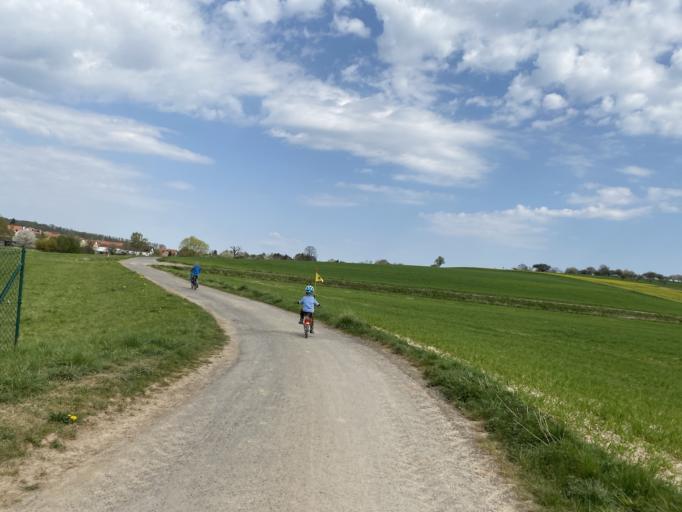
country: DE
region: Hesse
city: Budingen
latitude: 50.2498
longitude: 9.0699
